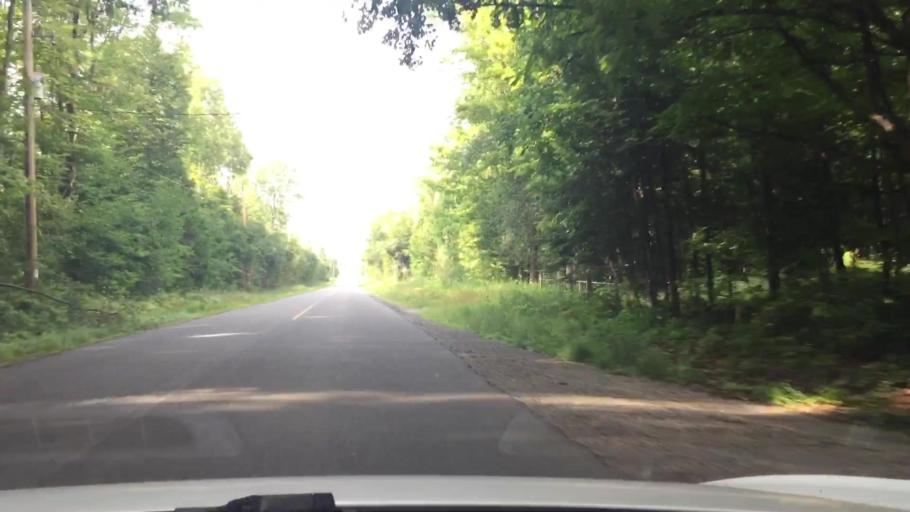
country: CA
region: Ontario
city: Oshawa
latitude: 43.9471
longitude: -78.7508
